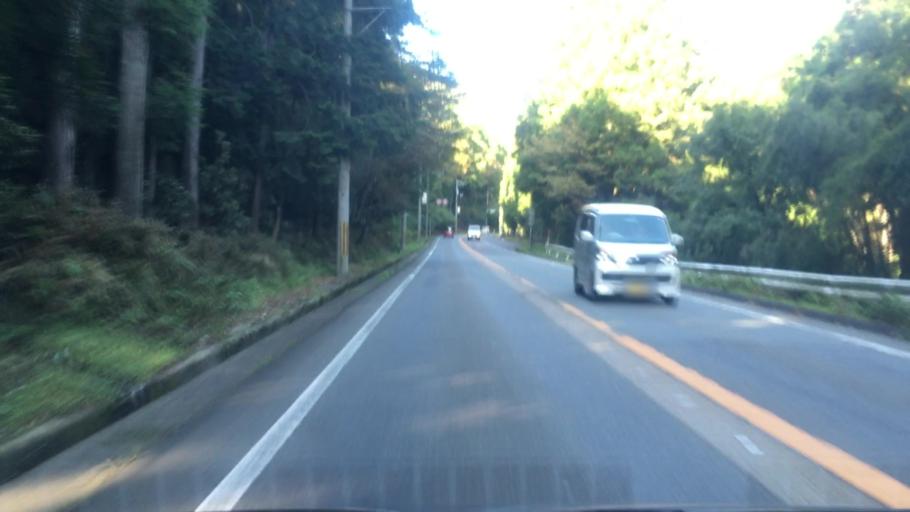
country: JP
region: Hyogo
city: Toyooka
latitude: 35.5793
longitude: 134.8563
